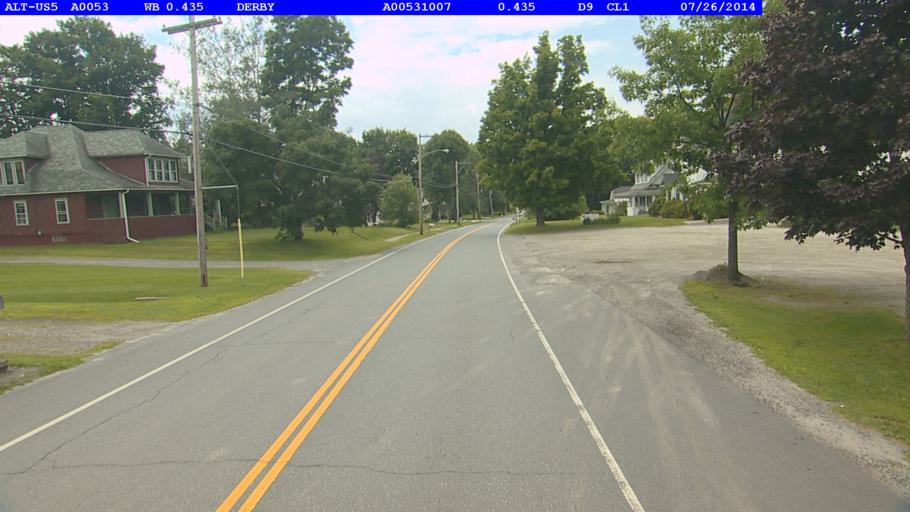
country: US
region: Vermont
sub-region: Orleans County
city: Newport
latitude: 45.0052
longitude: -72.0910
